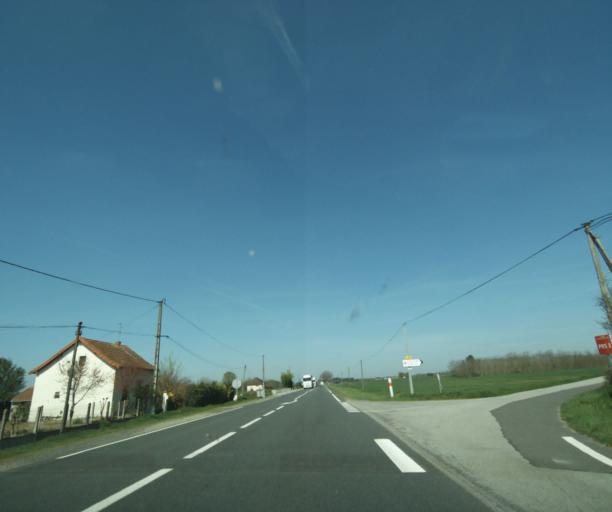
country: FR
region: Auvergne
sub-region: Departement de l'Allier
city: Trevol
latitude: 46.6673
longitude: 3.2406
